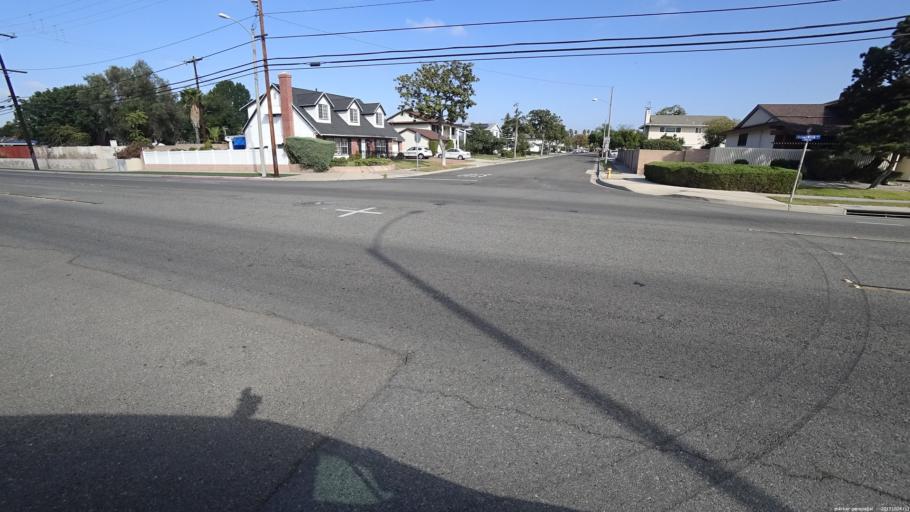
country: US
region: California
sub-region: Orange County
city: Garden Grove
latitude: 33.7959
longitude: -117.9339
